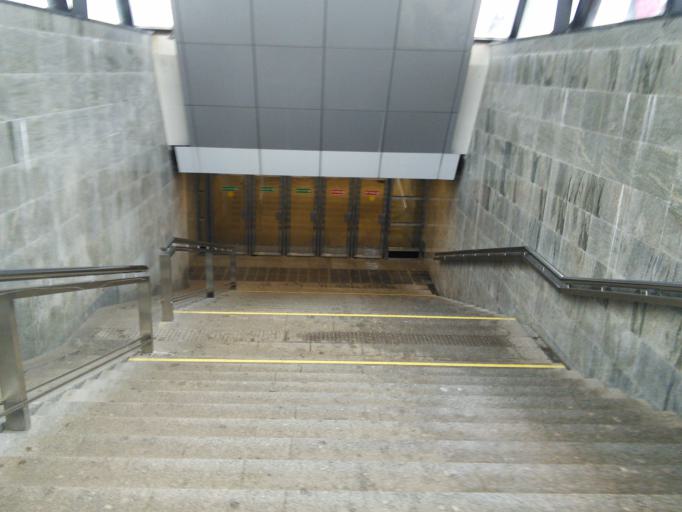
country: RU
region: Moscow
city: Brateyevo
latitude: 55.6321
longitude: 37.7669
